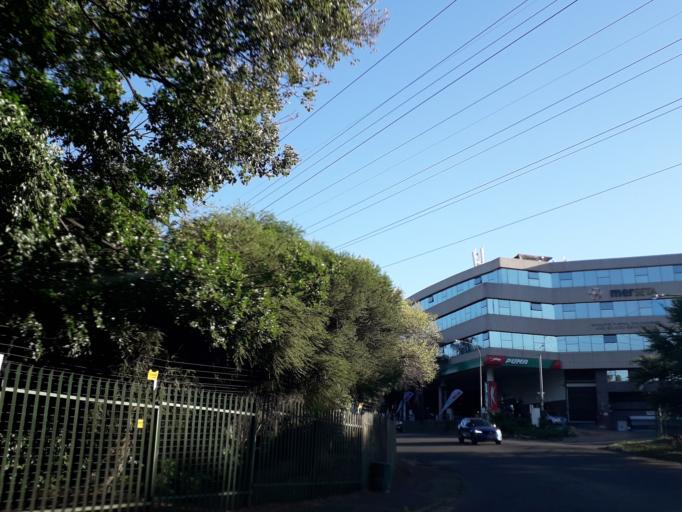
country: ZA
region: Gauteng
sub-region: City of Johannesburg Metropolitan Municipality
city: Johannesburg
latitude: -26.1729
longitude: 28.0130
